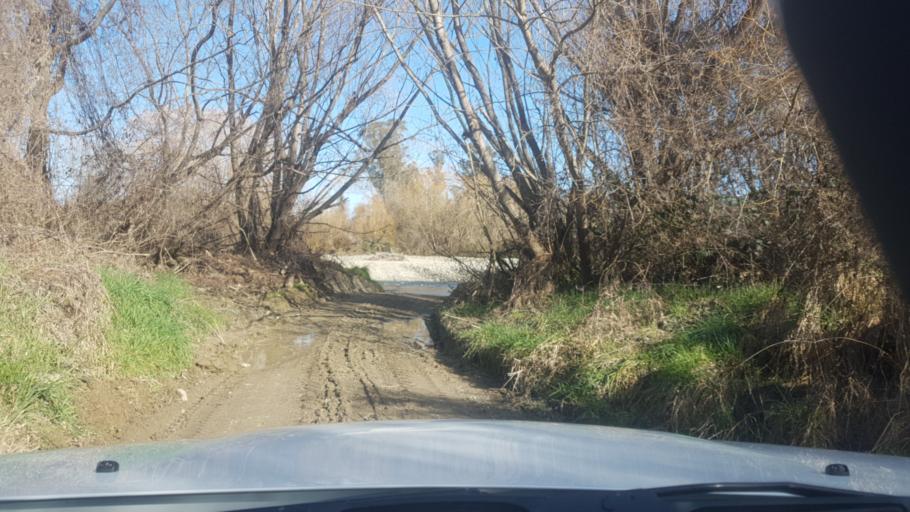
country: NZ
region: Canterbury
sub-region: Timaru District
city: Pleasant Point
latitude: -44.1714
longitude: 171.2350
